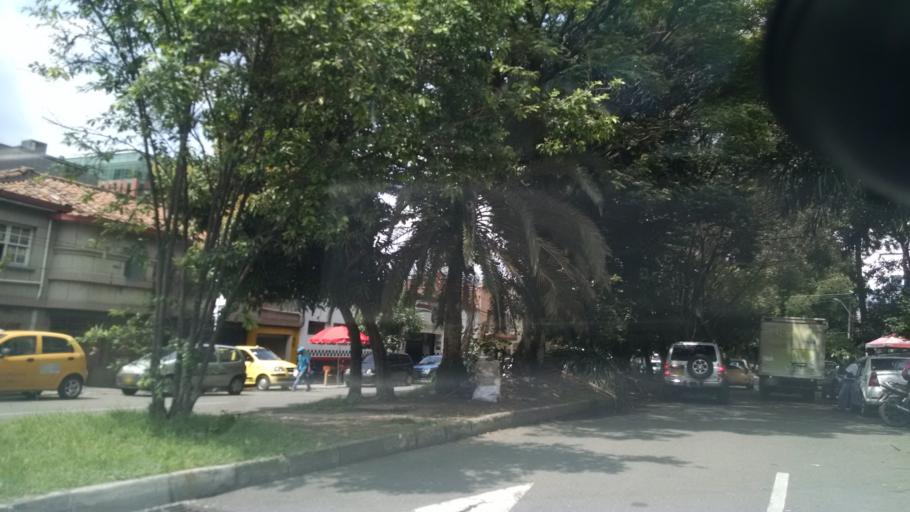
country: CO
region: Antioquia
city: Medellin
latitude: 6.2643
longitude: -75.5653
